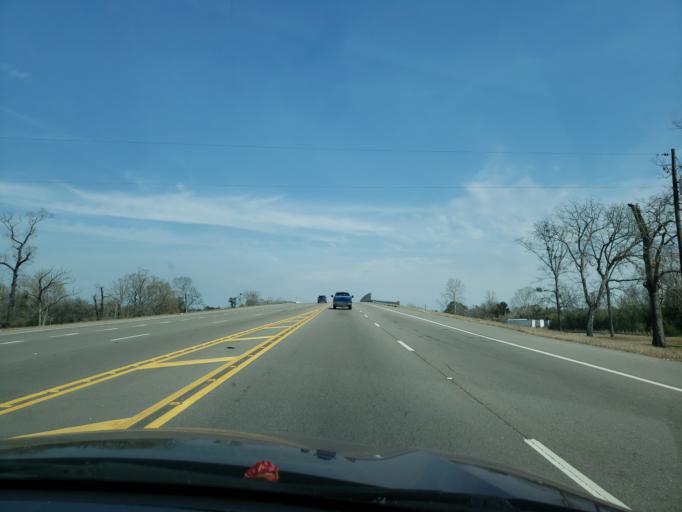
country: US
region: Alabama
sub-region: Elmore County
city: Elmore
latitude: 32.5374
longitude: -86.3168
